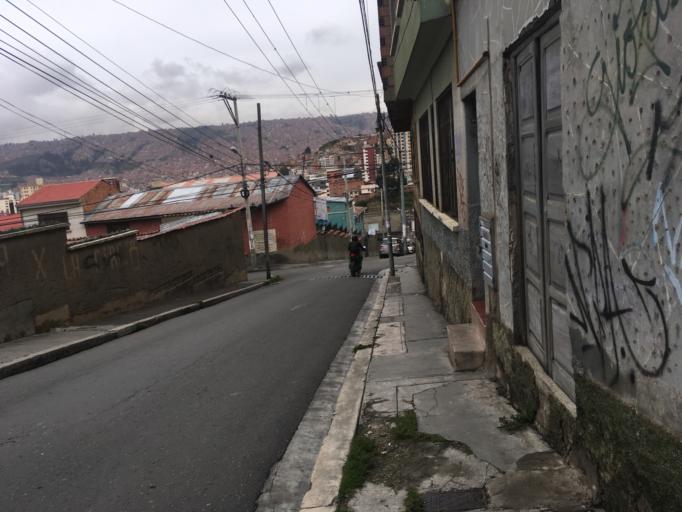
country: BO
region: La Paz
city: La Paz
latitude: -16.4922
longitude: -68.1165
